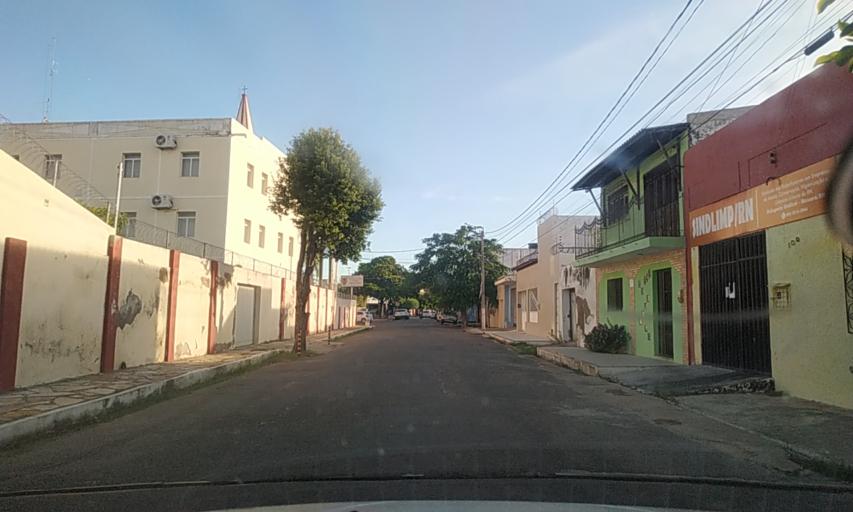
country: BR
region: Rio Grande do Norte
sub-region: Mossoro
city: Mossoro
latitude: -5.1929
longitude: -37.3399
